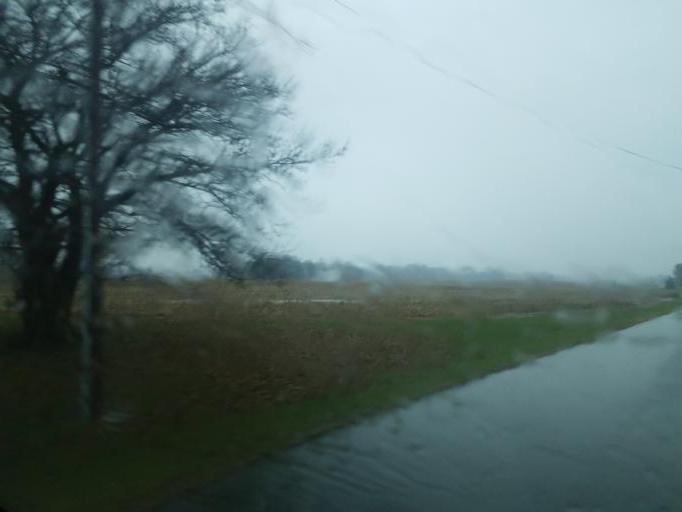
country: US
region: Ohio
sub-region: Delaware County
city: Ashley
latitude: 40.3597
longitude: -82.8720
